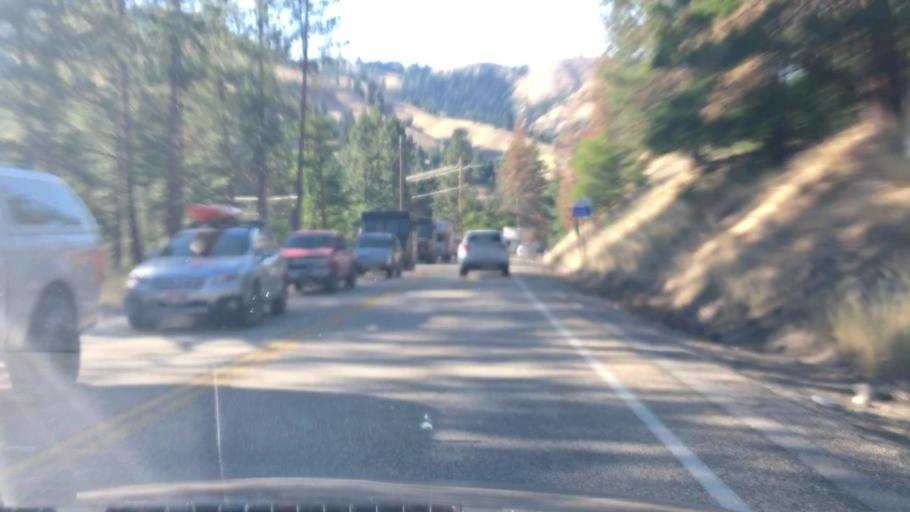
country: US
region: Idaho
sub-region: Boise County
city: Idaho City
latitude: 44.0495
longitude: -116.1324
